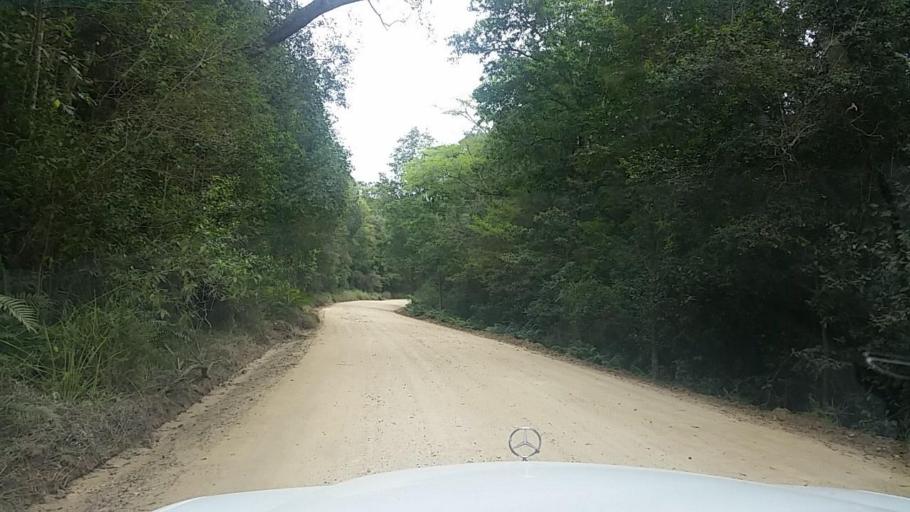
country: ZA
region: Western Cape
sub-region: Eden District Municipality
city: Knysna
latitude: -33.9490
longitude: 23.1503
